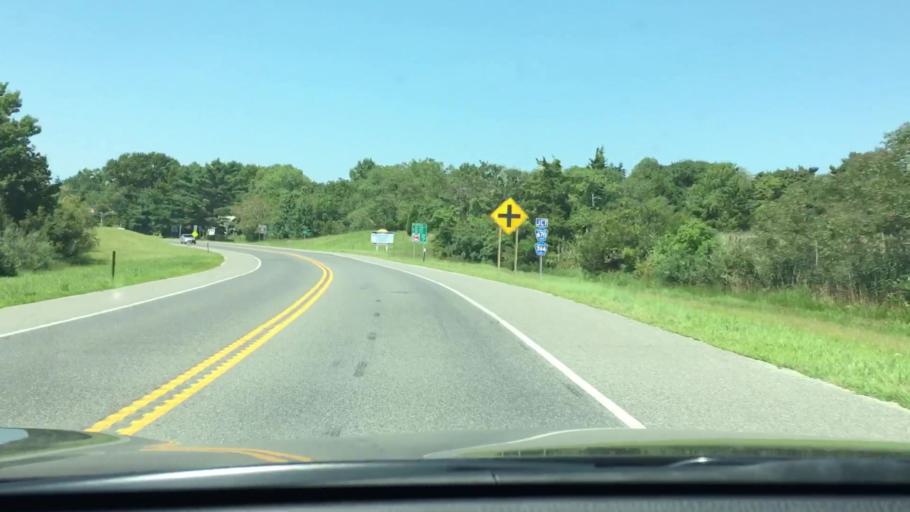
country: US
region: New Jersey
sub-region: Cumberland County
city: Port Norris
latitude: 39.2895
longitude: -74.9924
